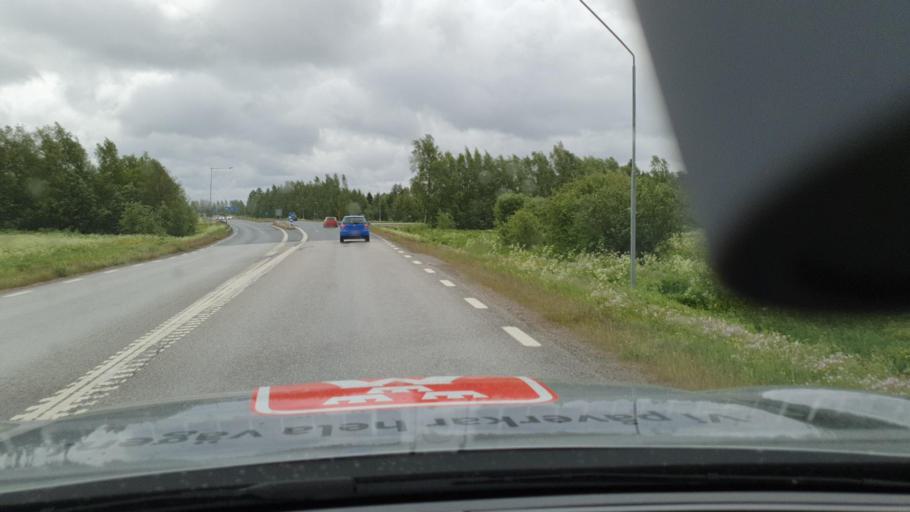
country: SE
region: Norrbotten
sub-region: Haparanda Kommun
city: Haparanda
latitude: 65.8498
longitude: 24.1194
